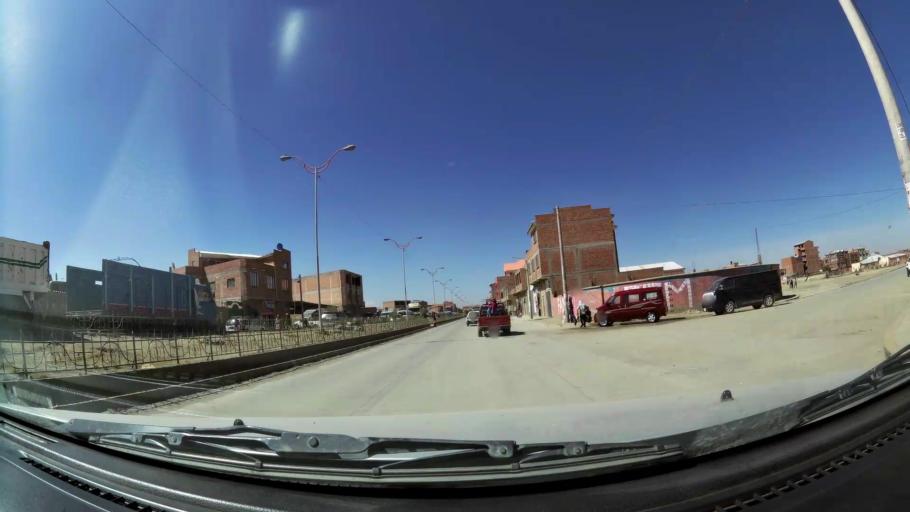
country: BO
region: La Paz
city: La Paz
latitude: -16.4989
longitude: -68.2291
